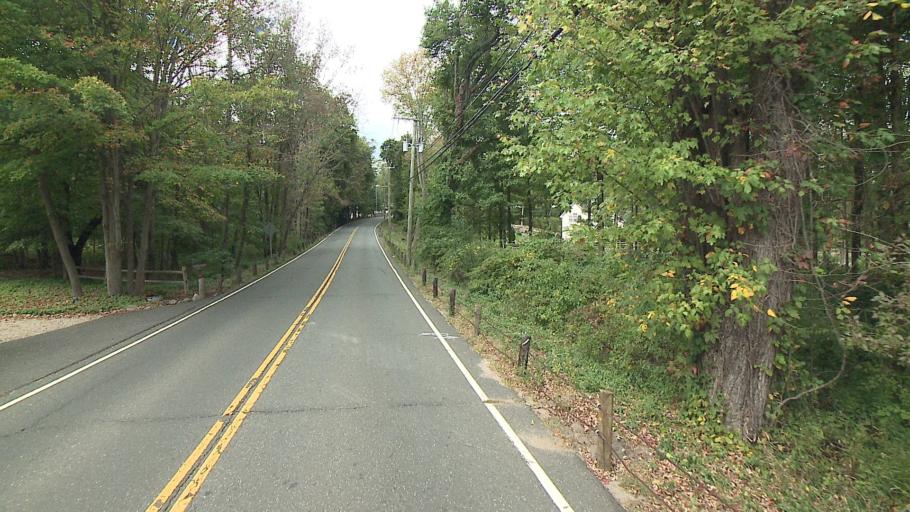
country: US
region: Connecticut
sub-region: Fairfield County
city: Ridgefield
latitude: 41.2500
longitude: -73.4894
